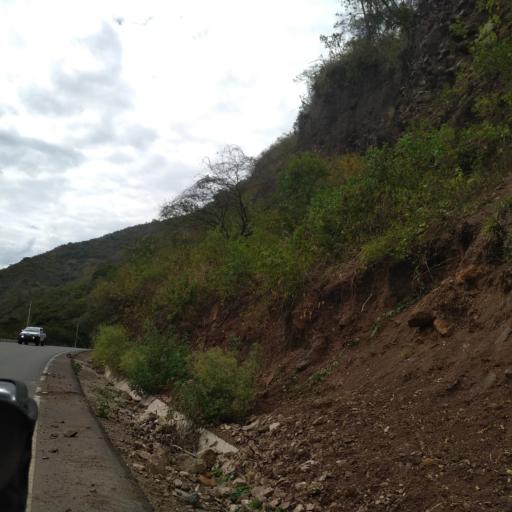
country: PE
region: Cajamarca
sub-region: Provincia de San Ignacio
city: Chirinos
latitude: -5.2343
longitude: -78.8668
